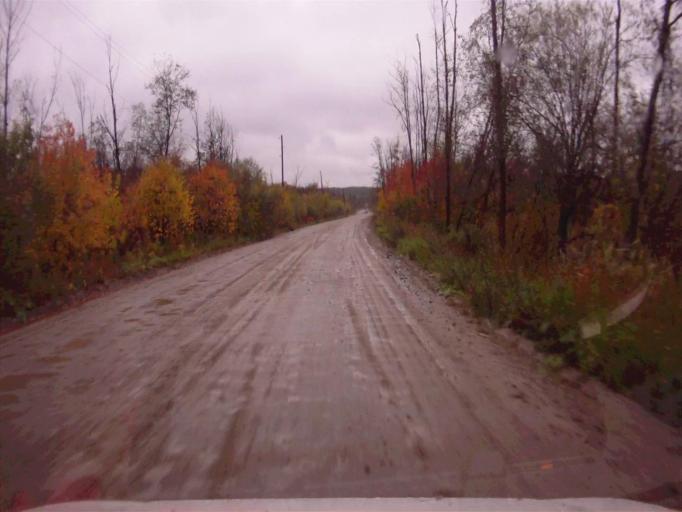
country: RU
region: Chelyabinsk
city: Kyshtym
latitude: 55.7340
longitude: 60.5169
